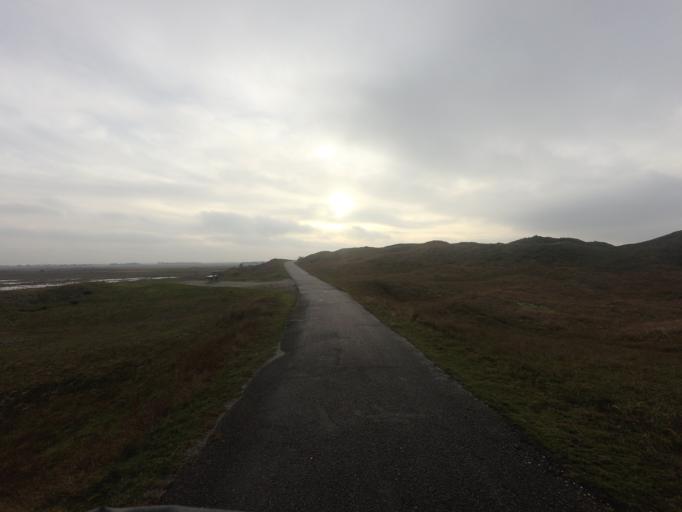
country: NL
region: North Holland
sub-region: Gemeente Texel
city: Den Burg
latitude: 53.1494
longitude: 4.8379
